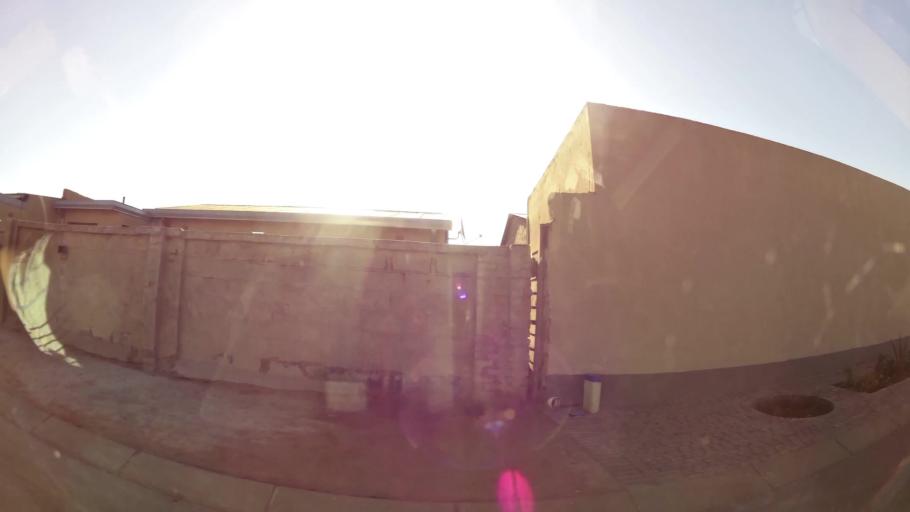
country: ZA
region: Gauteng
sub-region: Ekurhuleni Metropolitan Municipality
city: Tembisa
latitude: -26.0278
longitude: 28.2250
